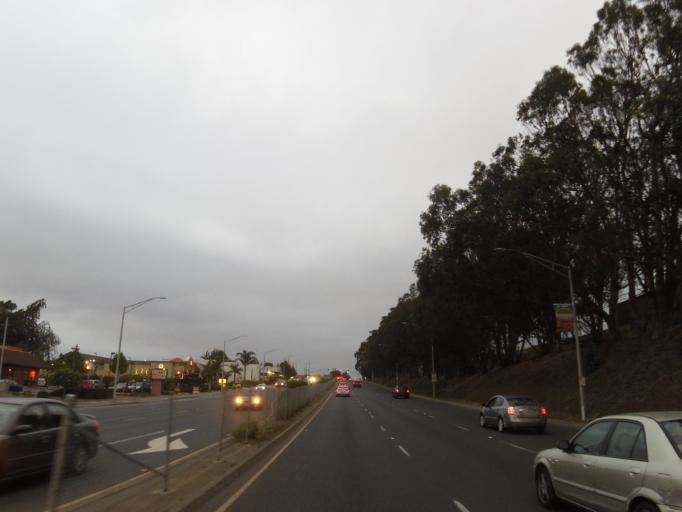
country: US
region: California
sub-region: San Mateo County
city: South San Francisco
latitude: 37.6461
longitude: -122.4276
